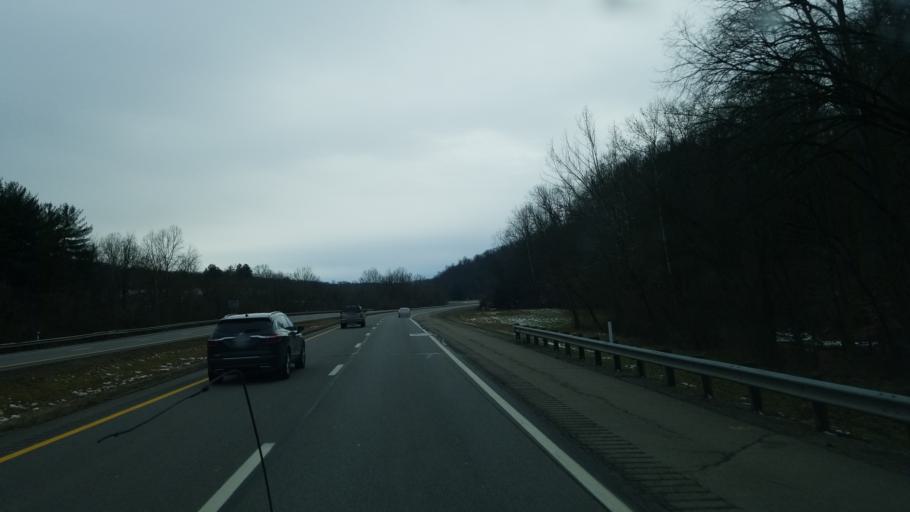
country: US
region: West Virginia
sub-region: Wood County
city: Mineral Wells
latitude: 39.1381
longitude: -81.5491
